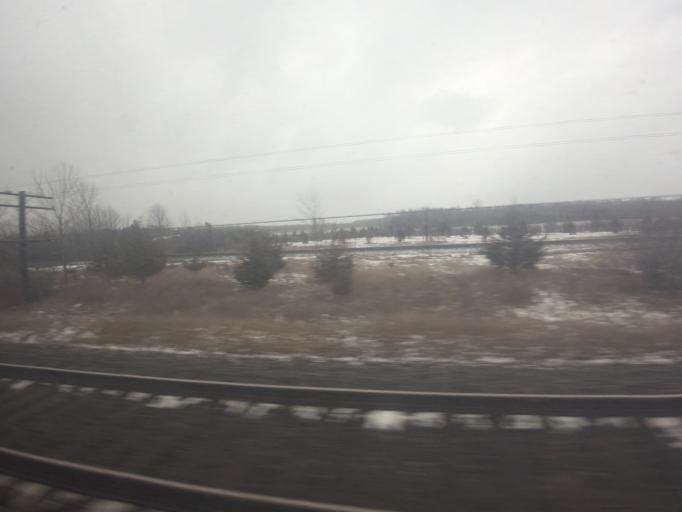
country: CA
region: Ontario
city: Quinte West
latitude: 44.0550
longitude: -77.6853
